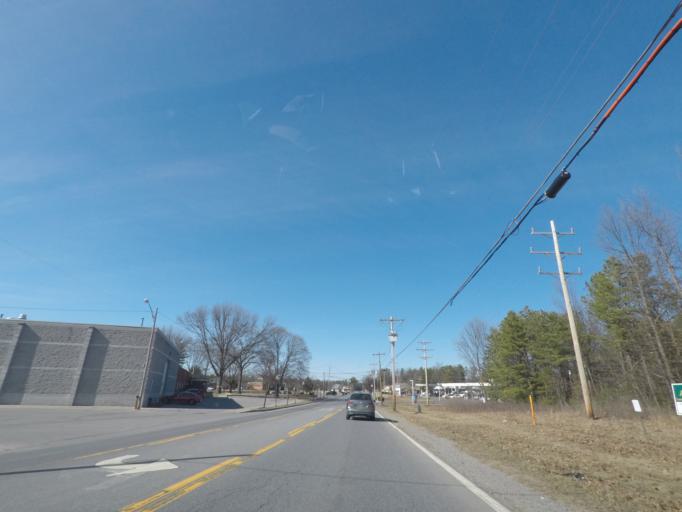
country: US
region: New York
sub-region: Saratoga County
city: Milton
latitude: 43.0443
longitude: -73.8503
